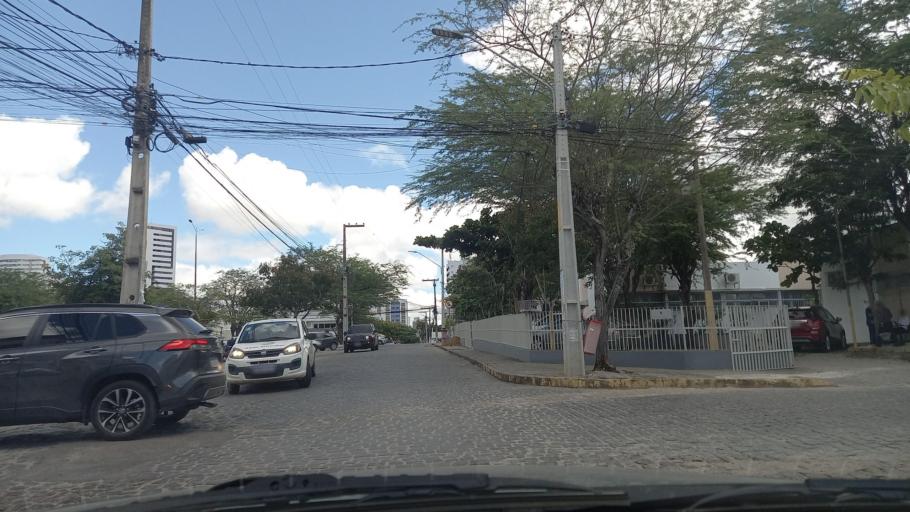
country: BR
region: Pernambuco
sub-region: Caruaru
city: Caruaru
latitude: -8.2674
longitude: -35.9634
